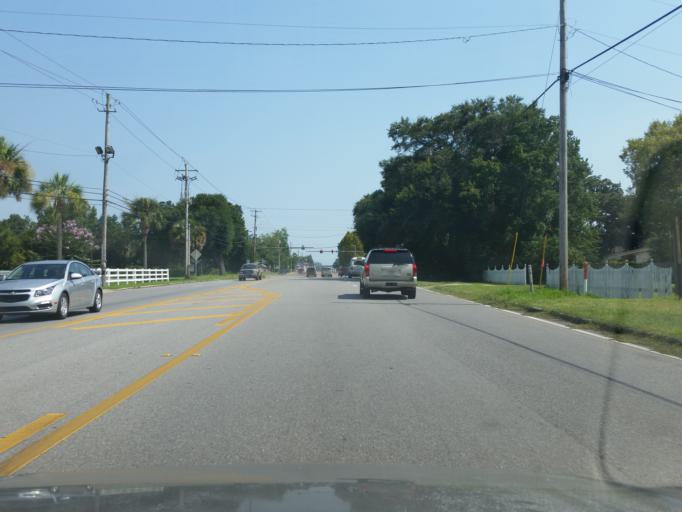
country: US
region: Florida
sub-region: Escambia County
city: Brent
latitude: 30.4774
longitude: -87.2463
